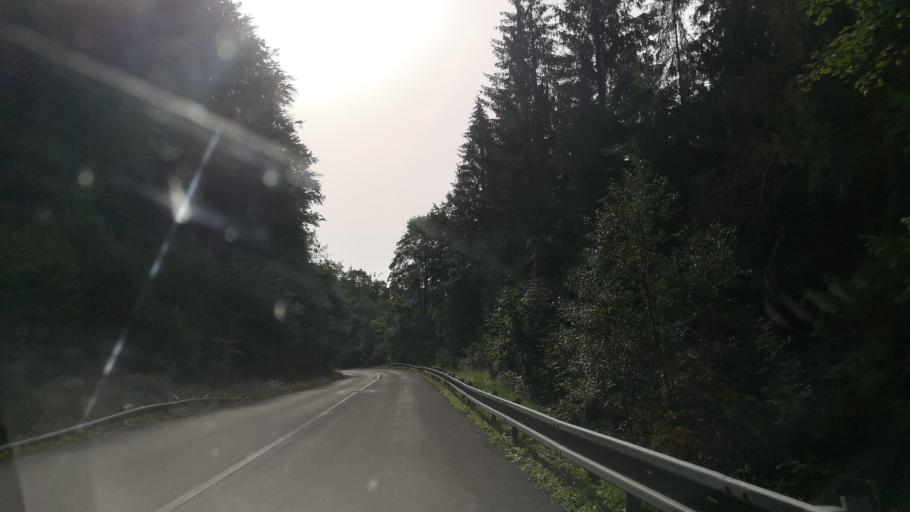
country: SK
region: Banskobystricky
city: Cierny Balog
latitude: 48.6006
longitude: 19.6985
